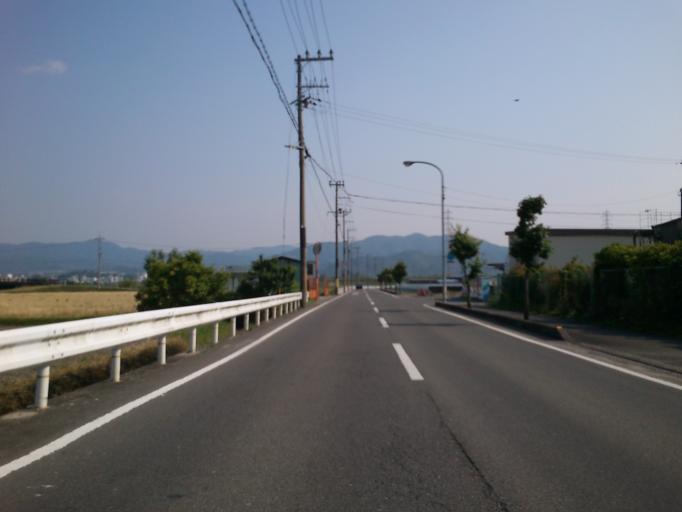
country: JP
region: Kyoto
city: Kameoka
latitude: 35.0334
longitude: 135.5741
